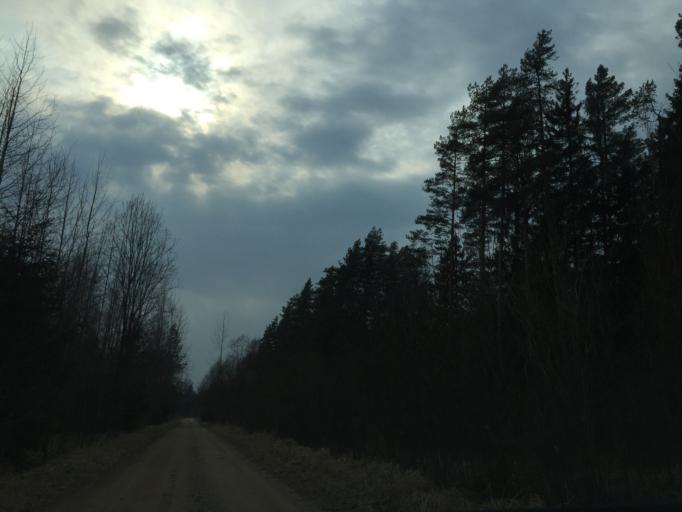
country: LV
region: Amatas Novads
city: Drabesi
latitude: 57.1995
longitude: 25.3777
